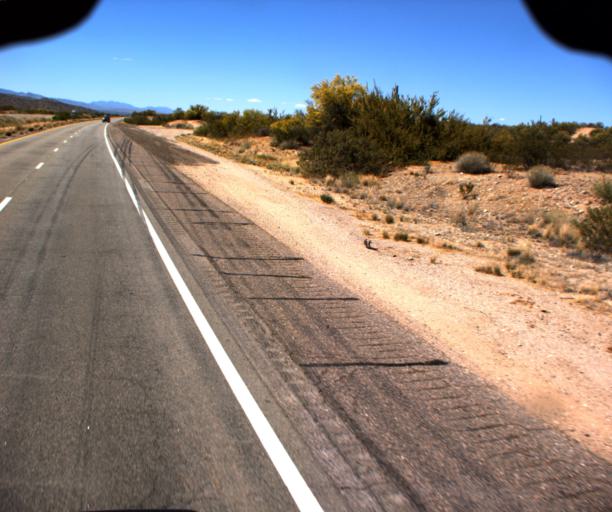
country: US
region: Arizona
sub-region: Yavapai County
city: Bagdad
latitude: 34.6473
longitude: -113.5694
